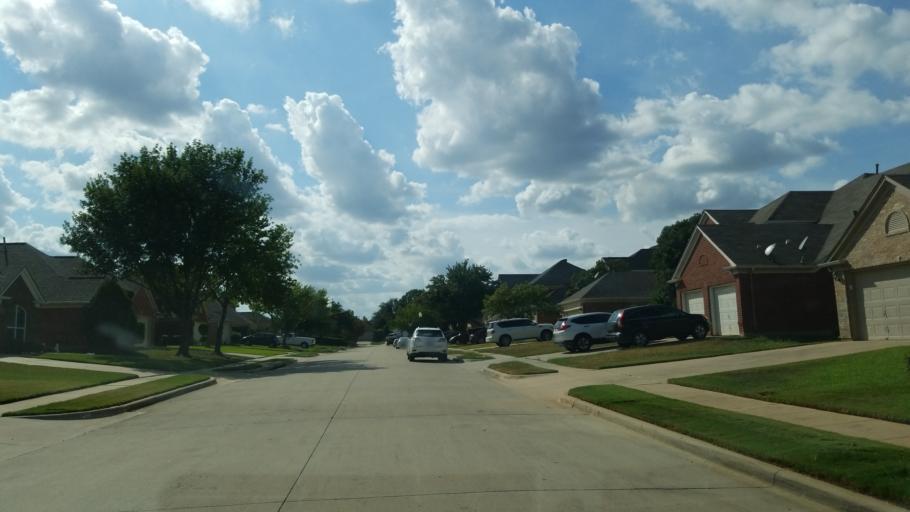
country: US
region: Texas
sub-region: Tarrant County
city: Euless
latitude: 32.8550
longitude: -97.0782
